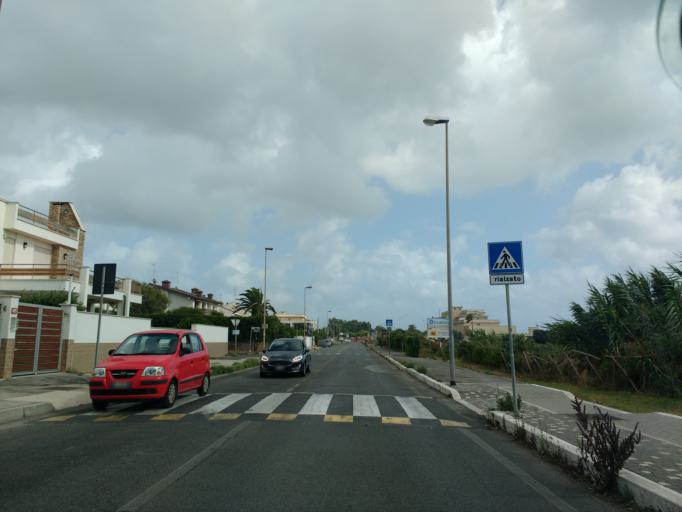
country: IT
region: Latium
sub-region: Citta metropolitana di Roma Capitale
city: Anzio
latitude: 41.4706
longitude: 12.6070
